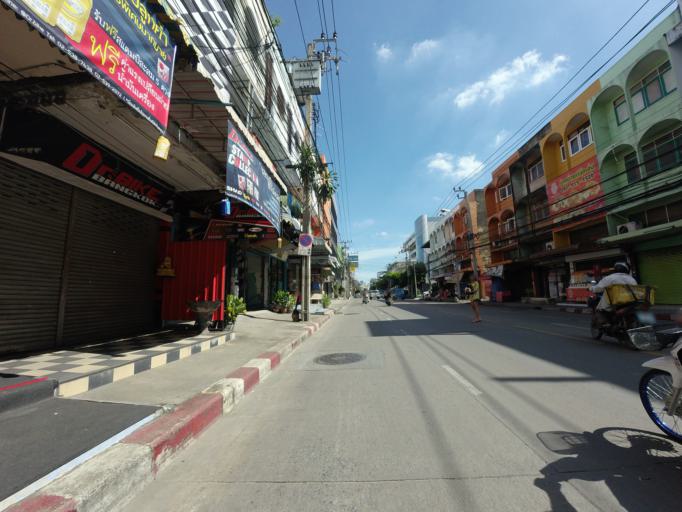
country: TH
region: Bangkok
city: Lat Phrao
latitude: 13.8032
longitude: 100.5966
